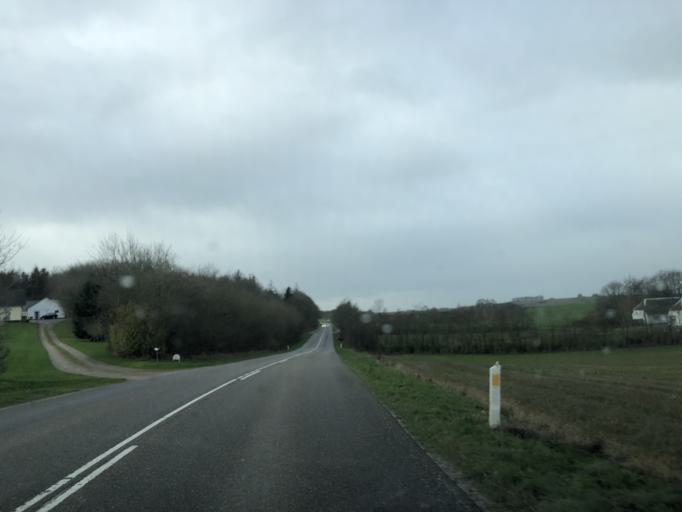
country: DK
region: North Denmark
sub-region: Rebild Kommune
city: Stovring
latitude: 56.8814
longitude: 9.7732
